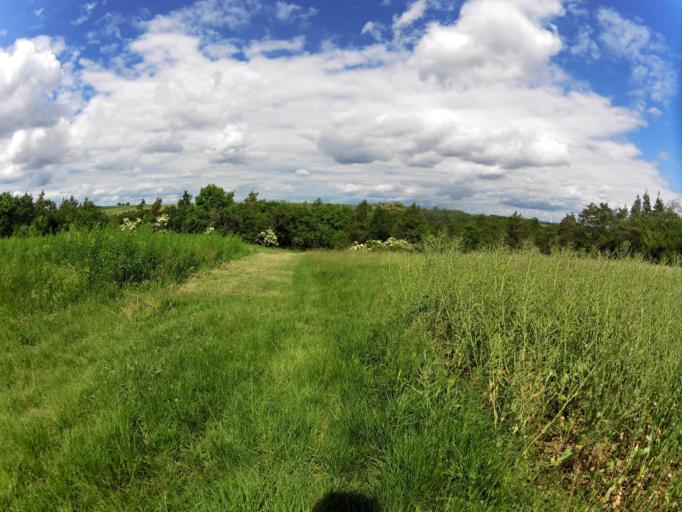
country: DE
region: Bavaria
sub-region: Regierungsbezirk Unterfranken
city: Sommerhausen
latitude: 49.6754
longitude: 10.0133
